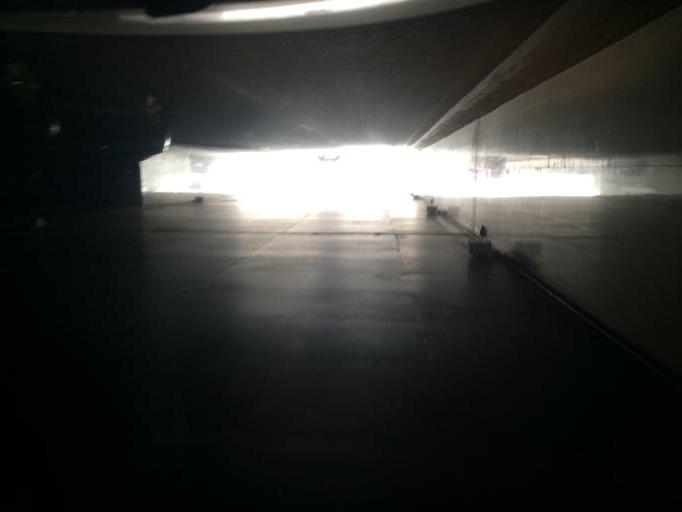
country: KZ
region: Astana Qalasy
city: Astana
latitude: 51.1340
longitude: 71.4101
